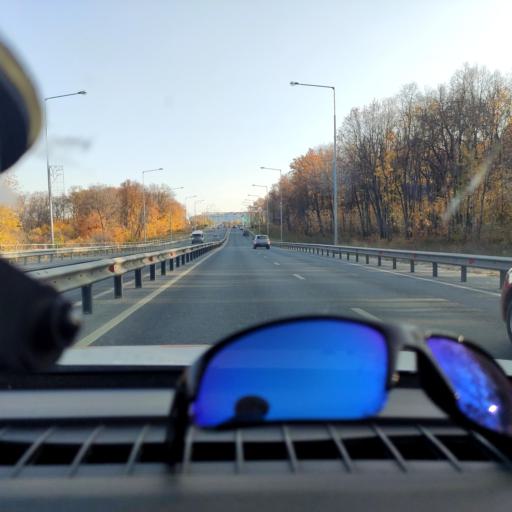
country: RU
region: Samara
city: Volzhskiy
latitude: 53.3585
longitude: 50.2068
